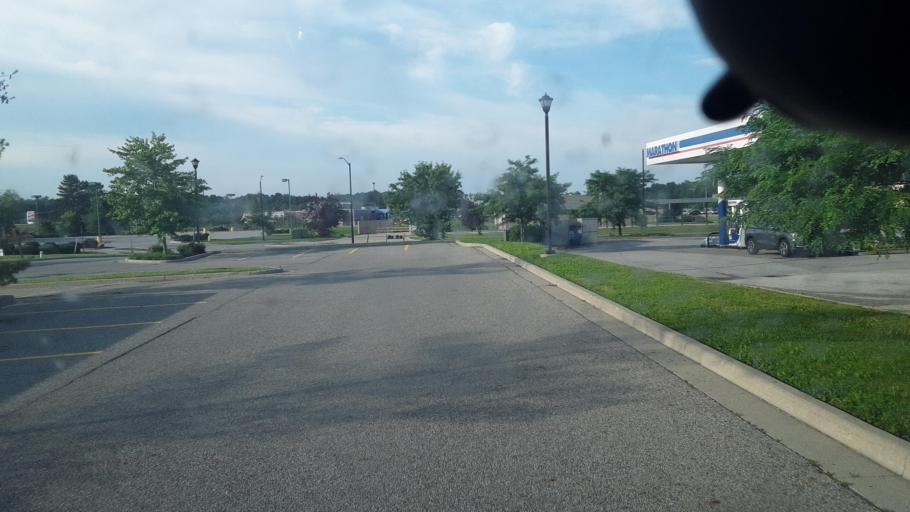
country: US
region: Indiana
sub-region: DeKalb County
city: Auburn
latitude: 41.3661
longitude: -85.0845
